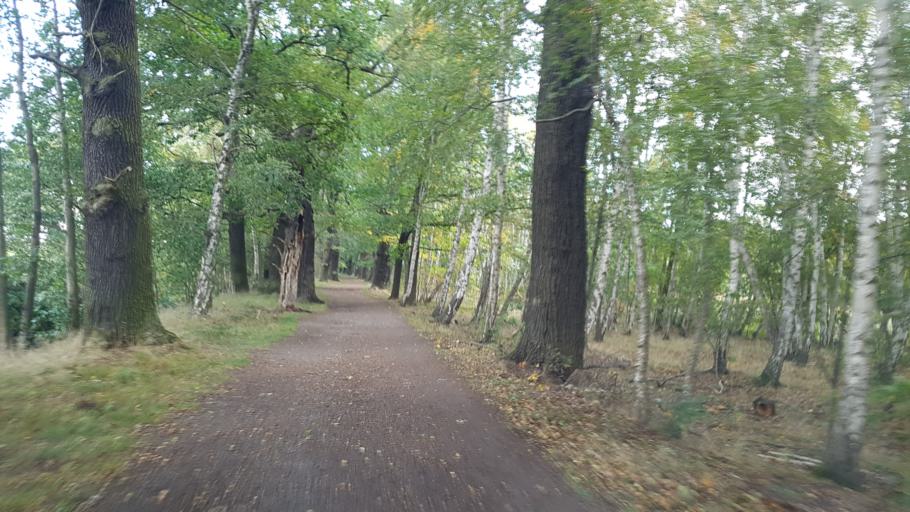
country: DE
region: Saxony
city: Dahlen
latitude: 51.3824
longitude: 12.9954
